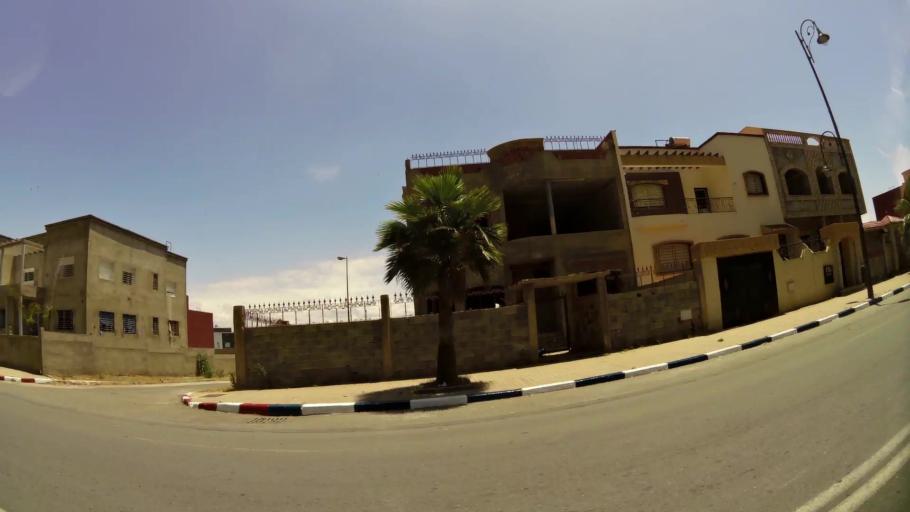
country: MA
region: Gharb-Chrarda-Beni Hssen
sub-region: Kenitra Province
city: Kenitra
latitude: 34.2686
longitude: -6.6426
